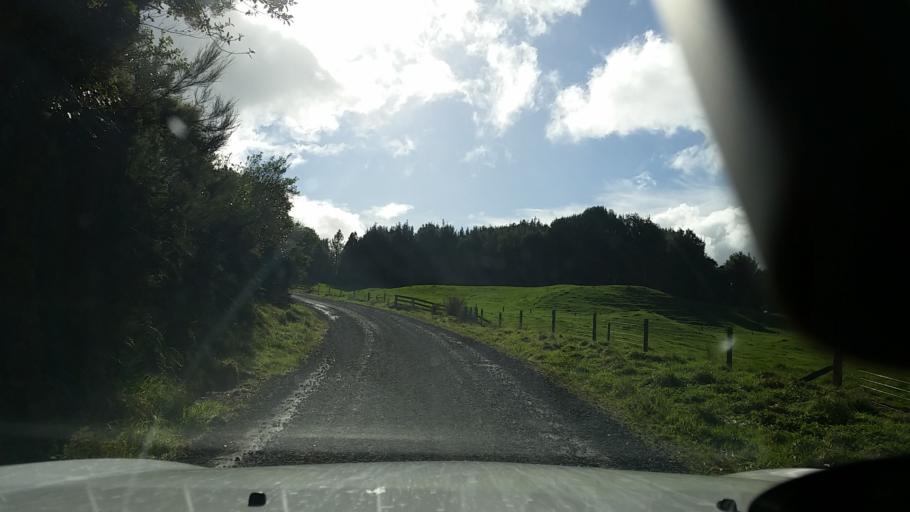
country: NZ
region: Bay of Plenty
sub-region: Rotorua District
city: Rotorua
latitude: -37.9892
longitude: 176.1773
